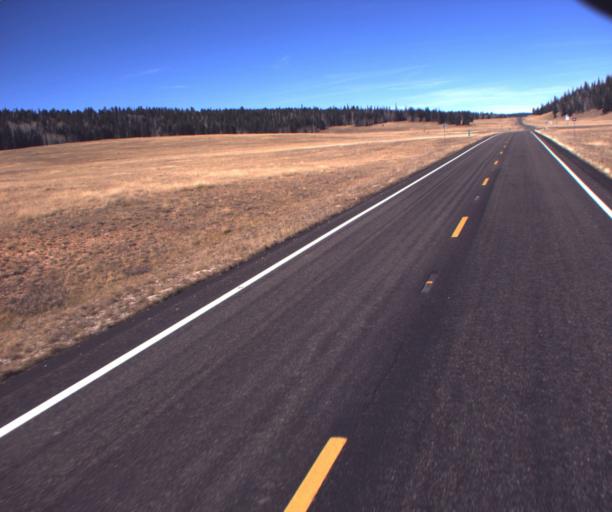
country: US
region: Arizona
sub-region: Coconino County
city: Grand Canyon
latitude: 36.3978
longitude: -112.1287
